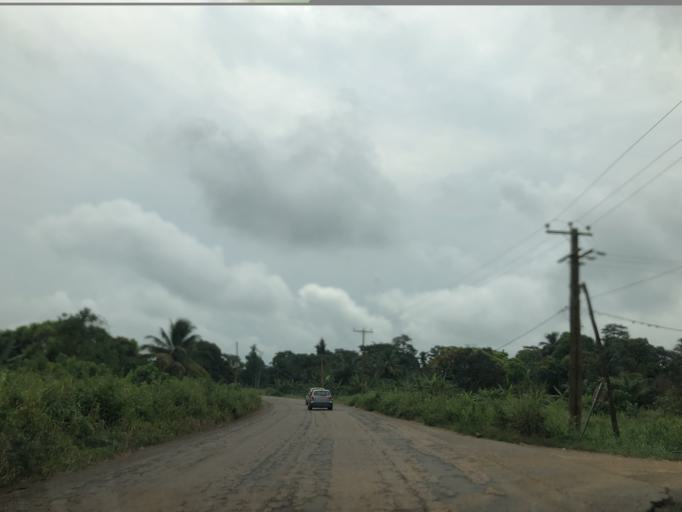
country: CM
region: Littoral
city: Dizangue
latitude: 3.4985
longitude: 10.1174
